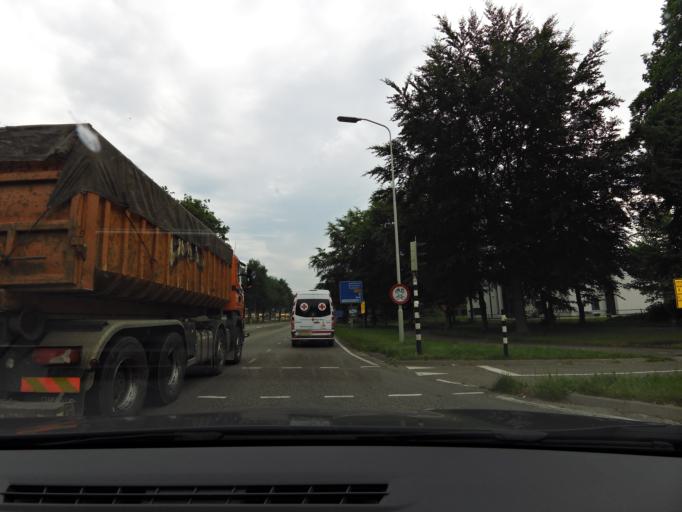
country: NL
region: Gelderland
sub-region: Gemeente Rheden
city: Dieren
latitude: 52.0408
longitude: 6.1005
